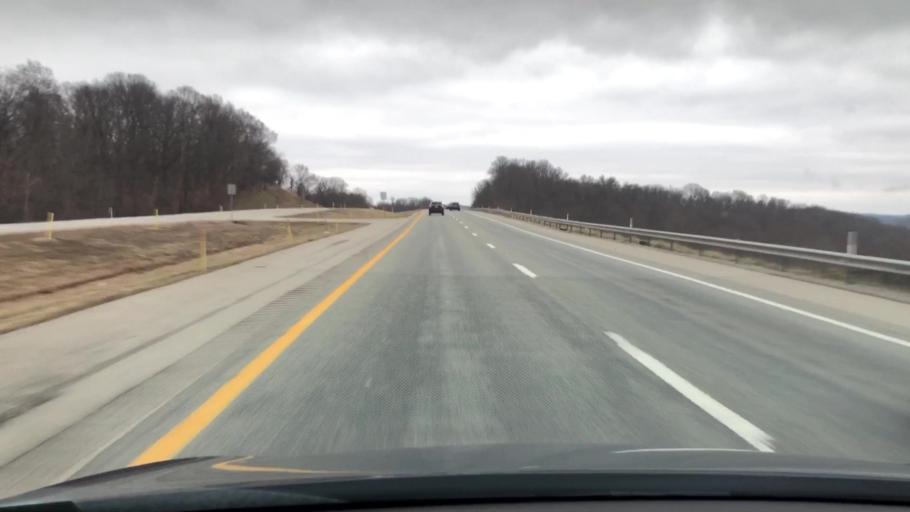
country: US
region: Pennsylvania
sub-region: Greene County
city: Morrisville
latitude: 39.8457
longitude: -80.1153
